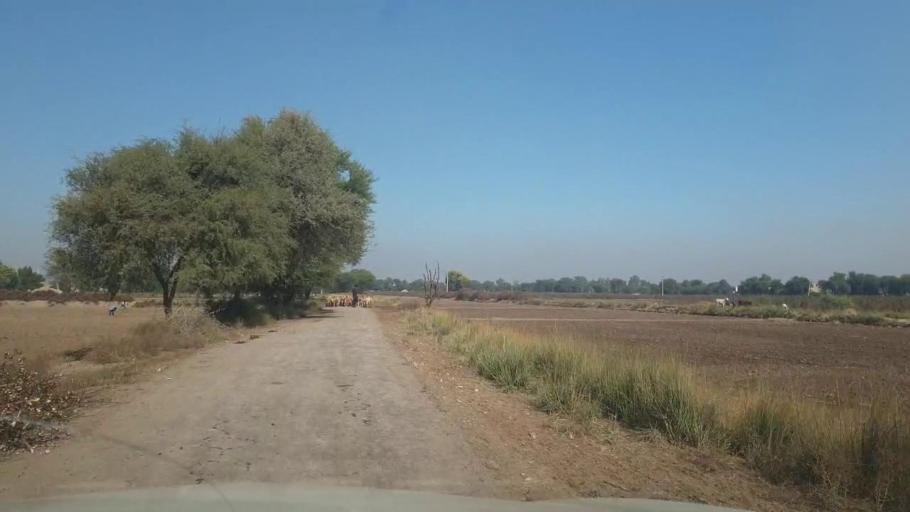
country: PK
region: Sindh
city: Bhan
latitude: 26.5818
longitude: 67.6999
